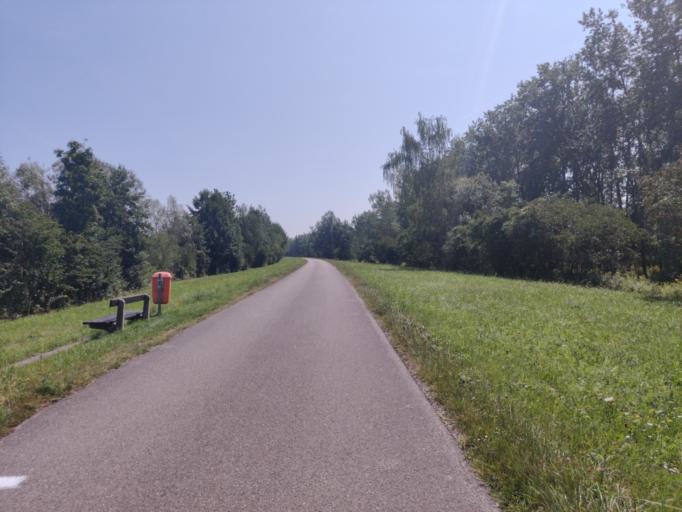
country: AT
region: Upper Austria
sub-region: Politischer Bezirk Urfahr-Umgebung
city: Feldkirchen an der Donau
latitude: 48.3275
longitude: 14.0379
